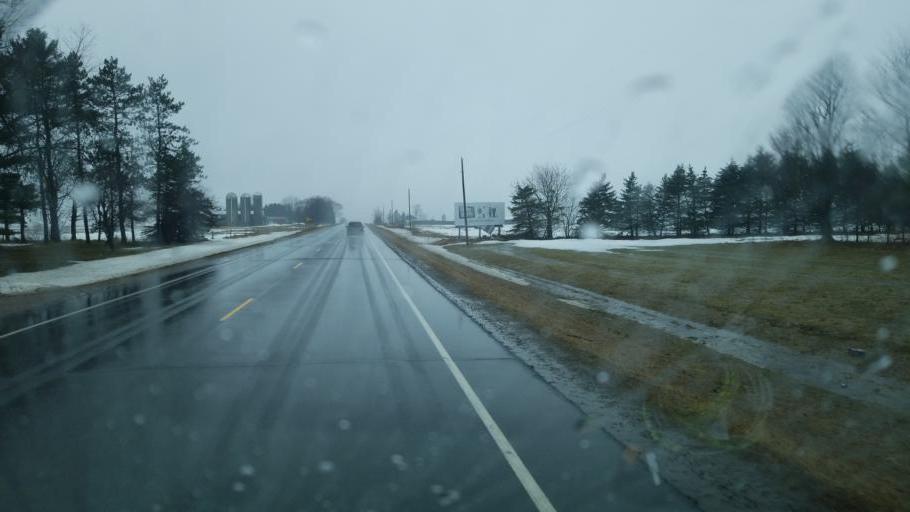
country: US
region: Wisconsin
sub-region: Marathon County
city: Spencer
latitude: 44.6562
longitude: -90.3256
